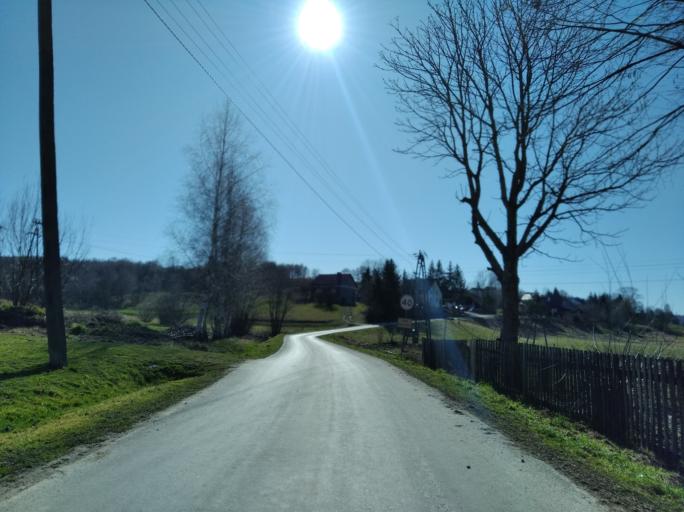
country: PL
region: Subcarpathian Voivodeship
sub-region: Powiat strzyzowski
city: Wisniowa
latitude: 49.9131
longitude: 21.7090
